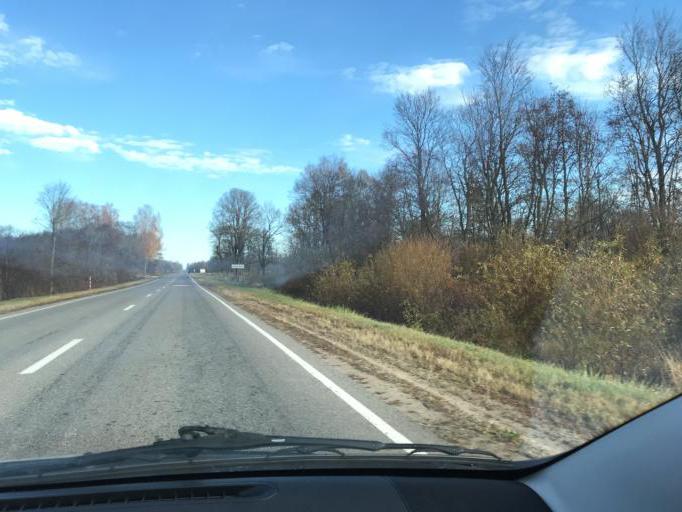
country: BY
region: Vitebsk
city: Haradok
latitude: 55.5226
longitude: 29.9717
